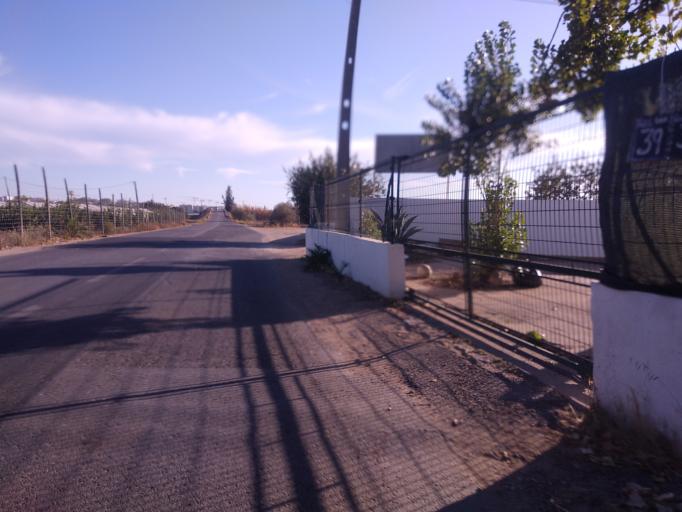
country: PT
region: Faro
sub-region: Faro
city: Faro
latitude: 37.0454
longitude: -7.9379
